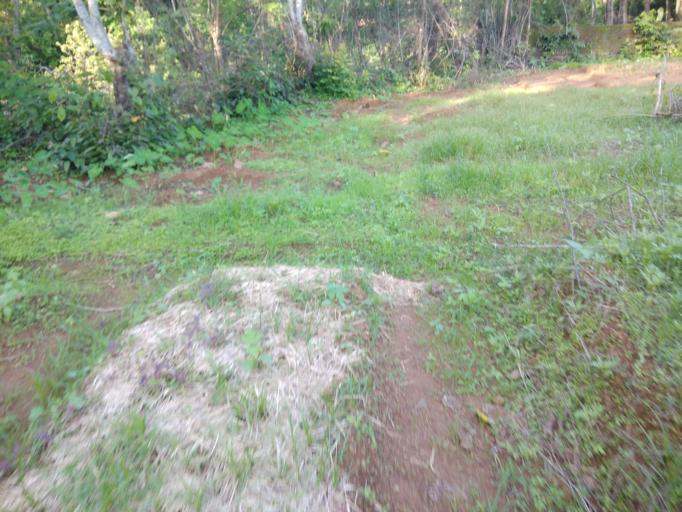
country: IN
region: Kerala
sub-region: Thrissur District
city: Avanoor
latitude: 10.5606
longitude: 76.1759
